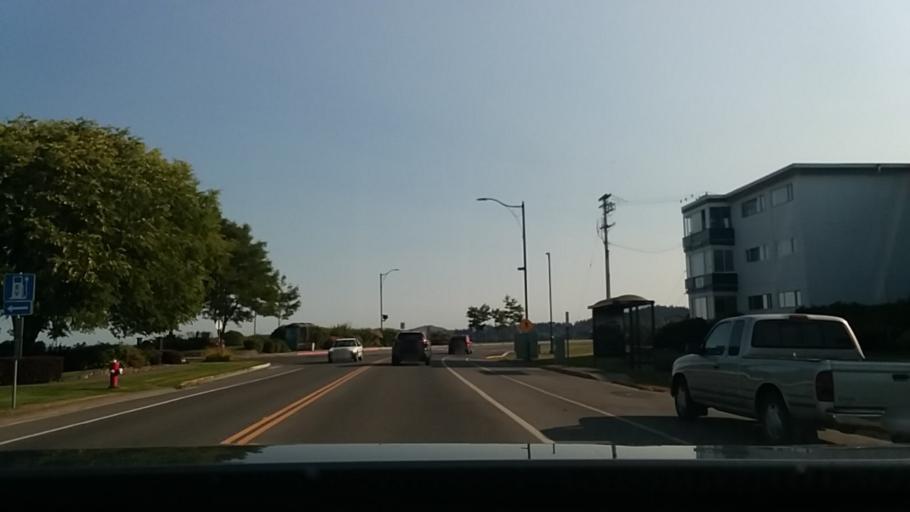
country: CA
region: British Columbia
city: North Saanich
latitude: 48.6420
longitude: -123.4004
